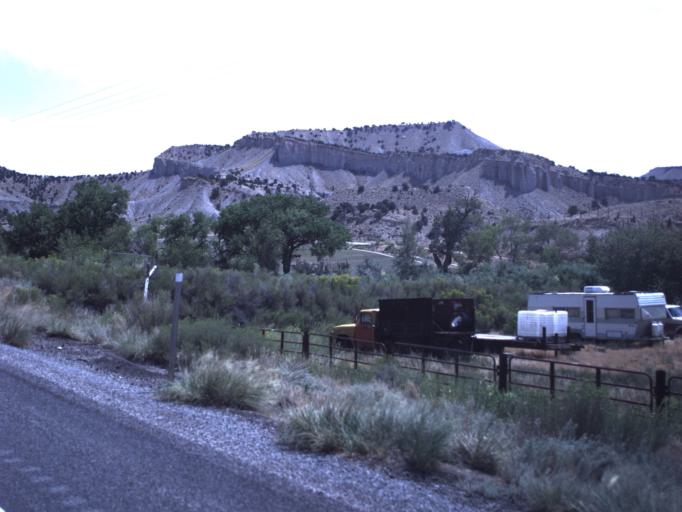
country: US
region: Utah
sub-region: Emery County
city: Huntington
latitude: 39.3569
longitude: -111.0287
